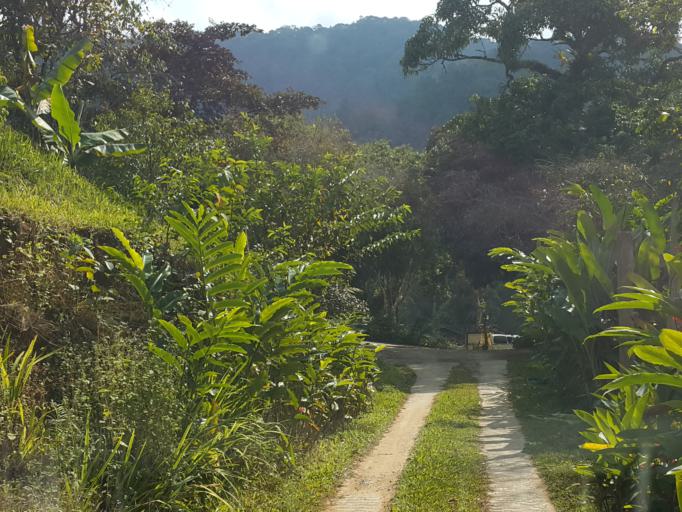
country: TH
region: Chiang Mai
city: Mae On
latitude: 18.9018
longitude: 99.3566
